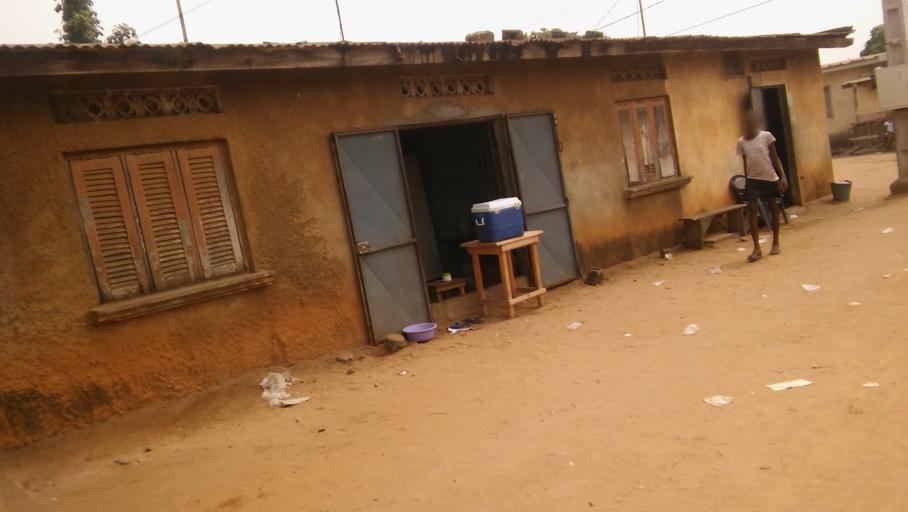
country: CI
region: Sud-Comoe
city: Grand-Bassam
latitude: 5.2139
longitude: -3.7343
